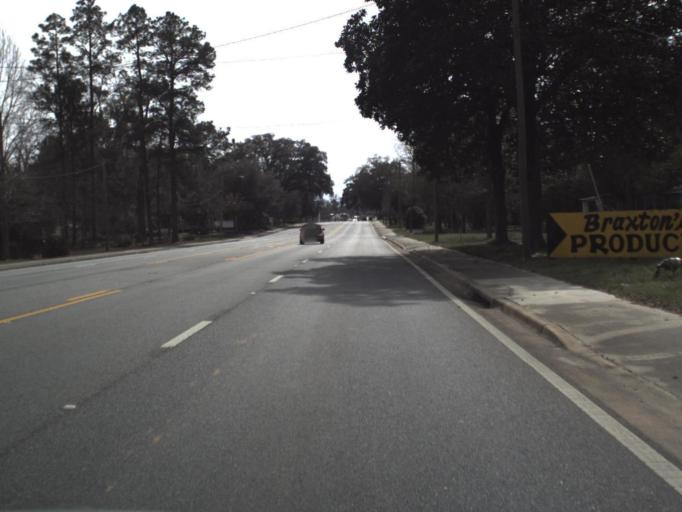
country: US
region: Florida
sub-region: Jackson County
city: Marianna
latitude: 30.8017
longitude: -85.3768
